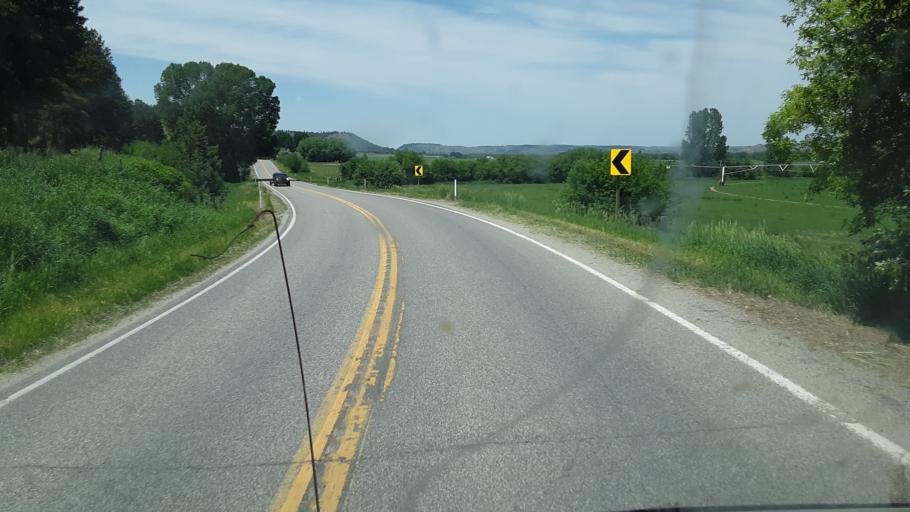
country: US
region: Montana
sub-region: Stillwater County
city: Columbus
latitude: 45.6032
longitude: -109.1996
